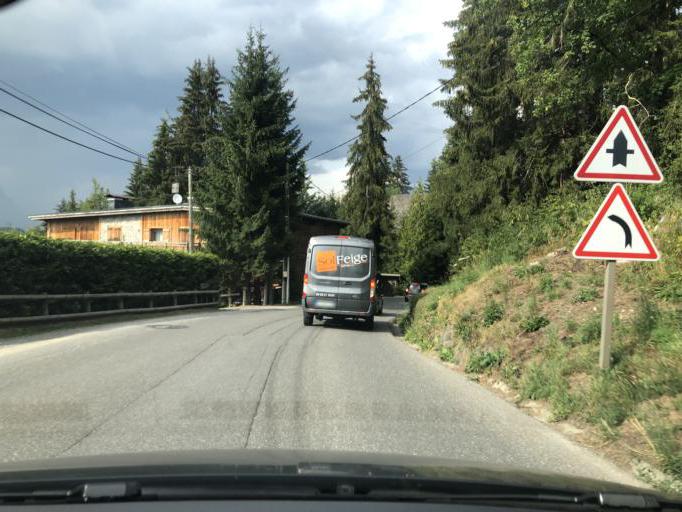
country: FR
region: Rhone-Alpes
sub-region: Departement de la Haute-Savoie
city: Megeve
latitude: 45.8646
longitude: 6.6327
